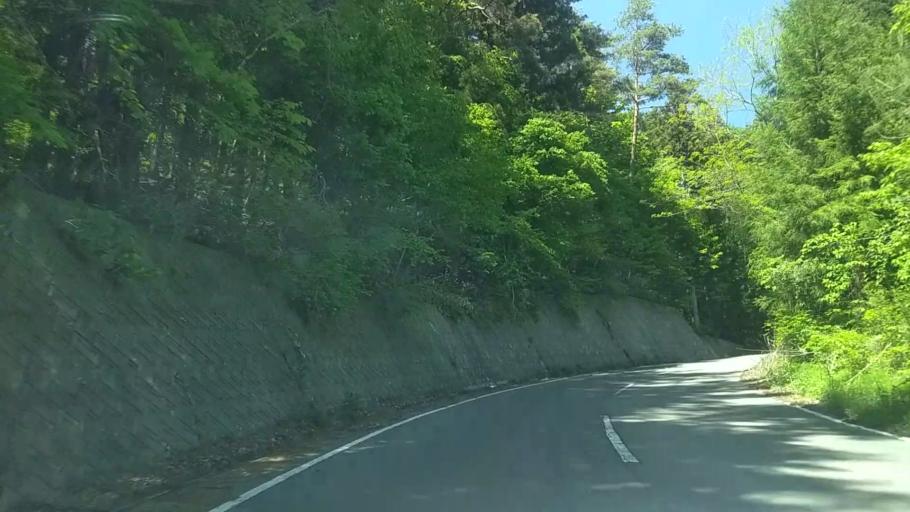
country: JP
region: Yamanashi
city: Nirasaki
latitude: 35.8638
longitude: 138.4475
